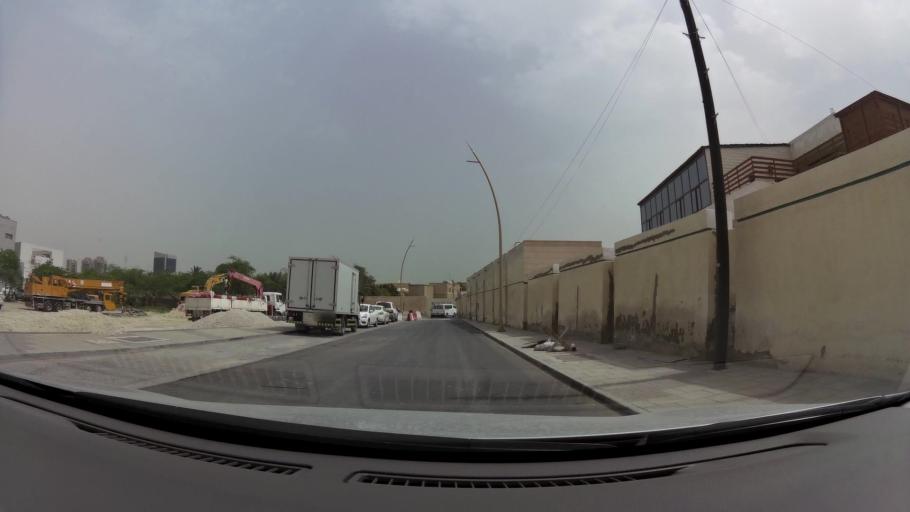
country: QA
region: Baladiyat ad Dawhah
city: Doha
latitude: 25.2680
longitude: 51.5067
